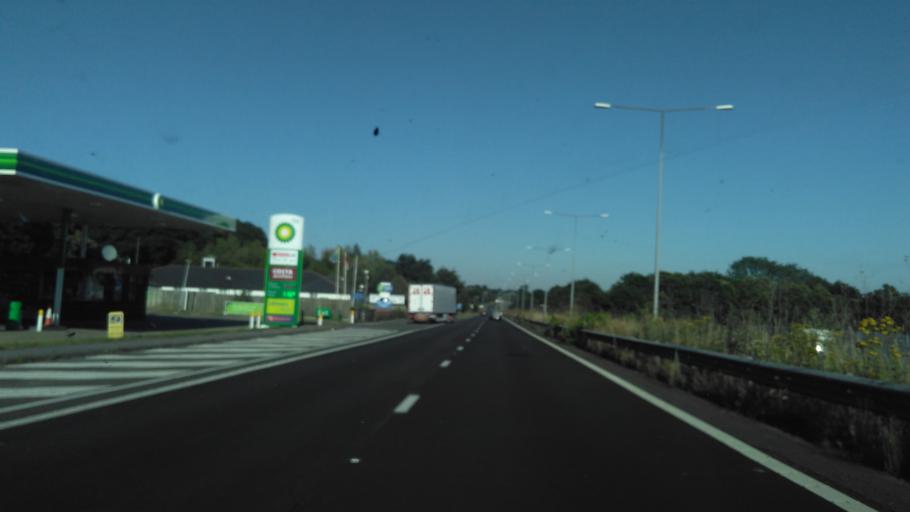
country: GB
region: England
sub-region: Kent
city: Dunkirk
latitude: 51.2877
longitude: 1.0106
